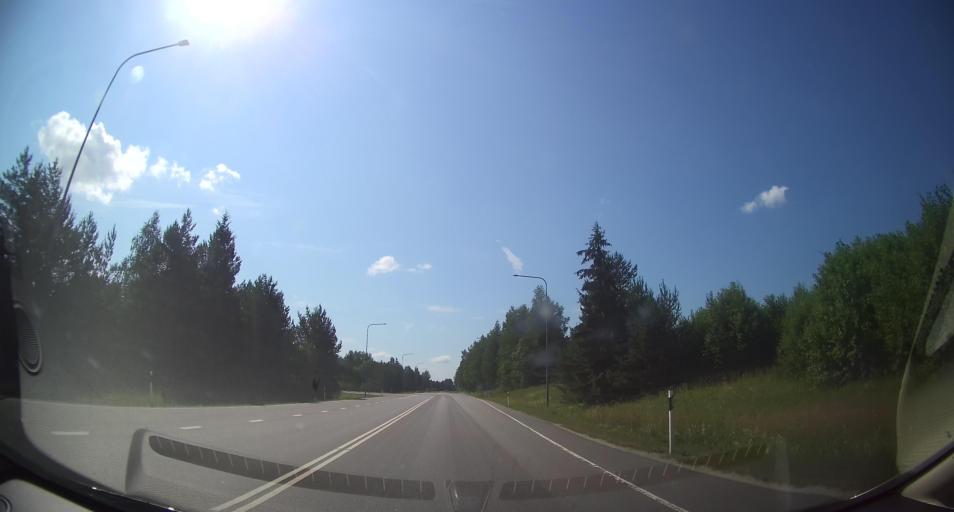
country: EE
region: Raplamaa
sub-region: Rapla vald
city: Rapla
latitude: 59.0903
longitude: 24.8013
